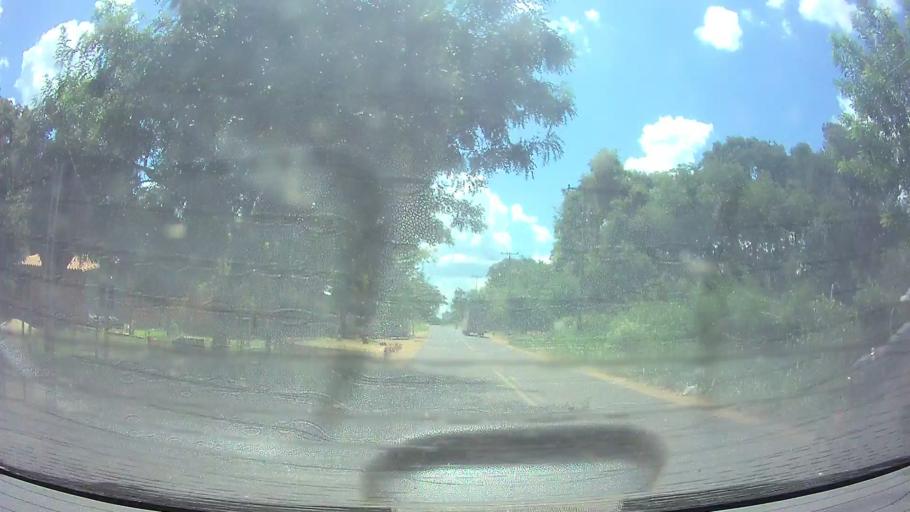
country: PY
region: Central
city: Limpio
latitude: -25.1716
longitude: -57.4433
